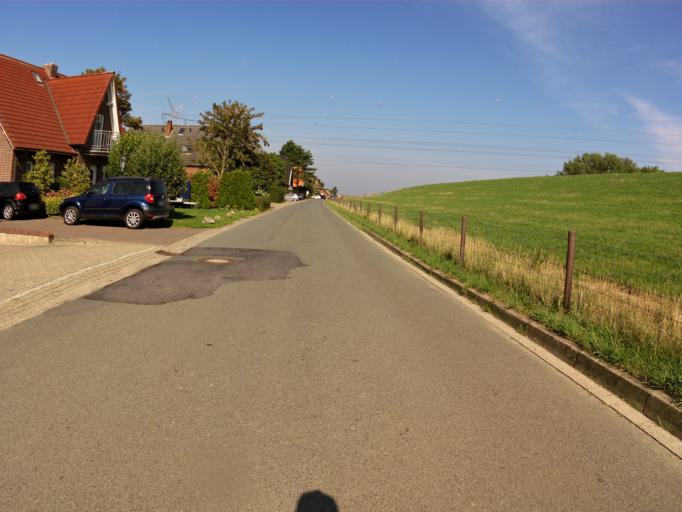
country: DE
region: Lower Saxony
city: Neuenkirchen
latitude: 53.1978
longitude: 8.4998
